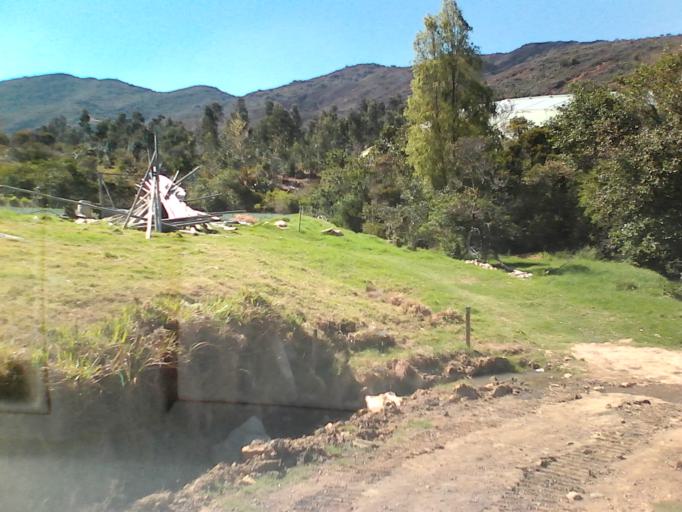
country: CO
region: Boyaca
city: Sachica
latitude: 5.5449
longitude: -73.5628
